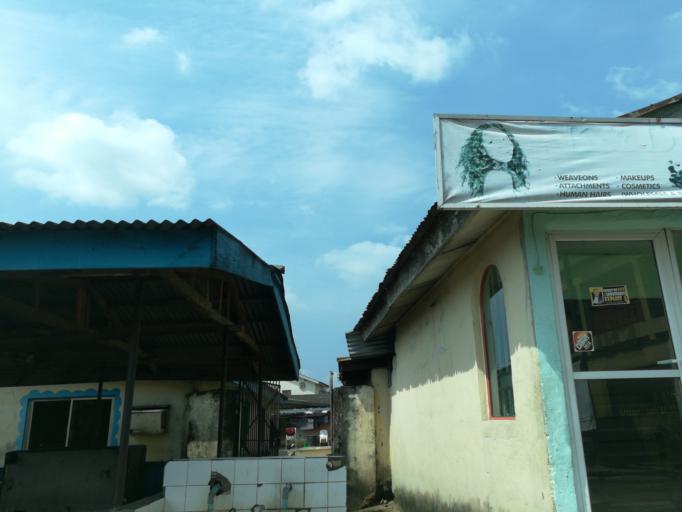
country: NG
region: Rivers
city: Port Harcourt
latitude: 4.8296
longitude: 6.9799
